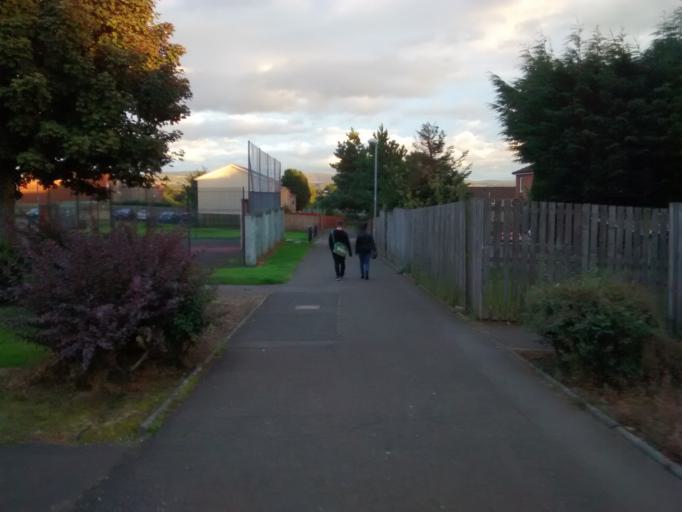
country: GB
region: Scotland
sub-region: West Lothian
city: Livingston
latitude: 55.8981
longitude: -3.5209
